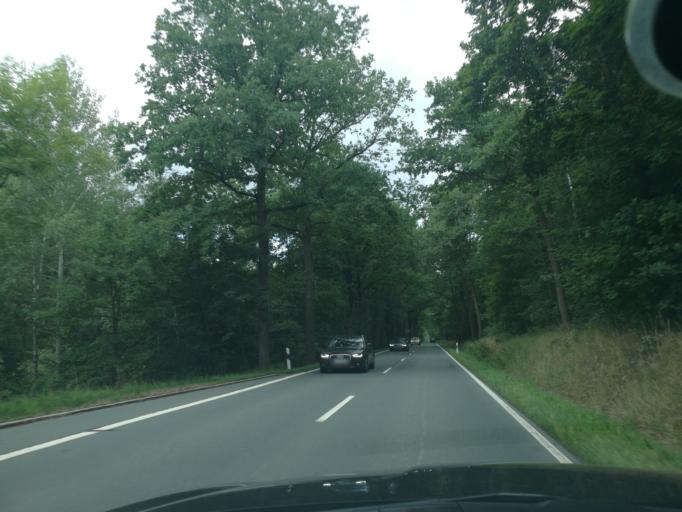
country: DE
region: Saxony
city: Eichigt
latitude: 50.3746
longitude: 12.2067
